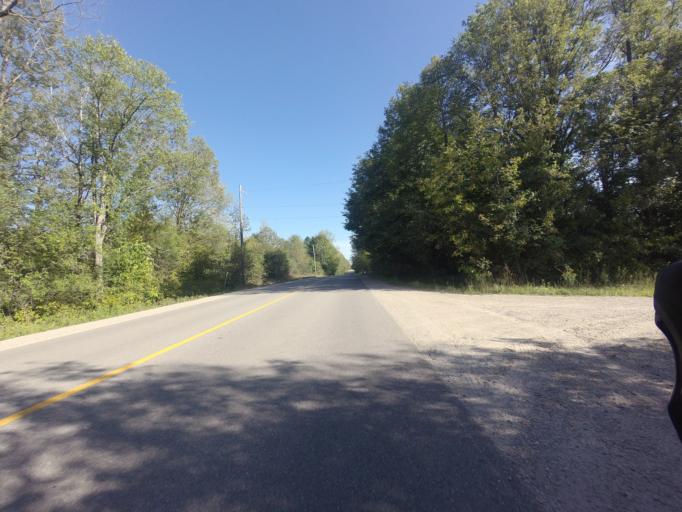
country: CA
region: Ontario
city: Perth
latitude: 44.9071
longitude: -76.3388
